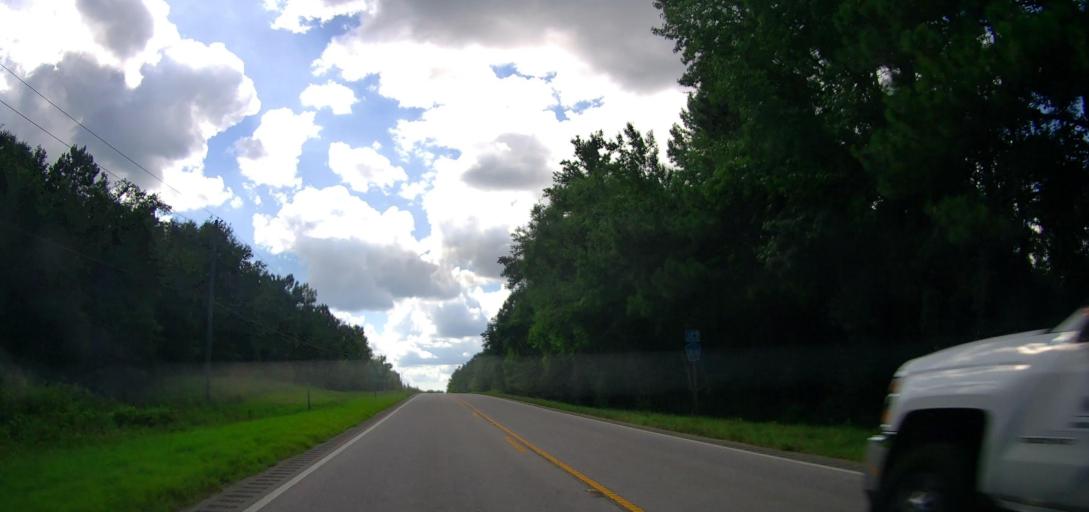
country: US
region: Alabama
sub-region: Lee County
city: Auburn
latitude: 32.4441
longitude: -85.5019
